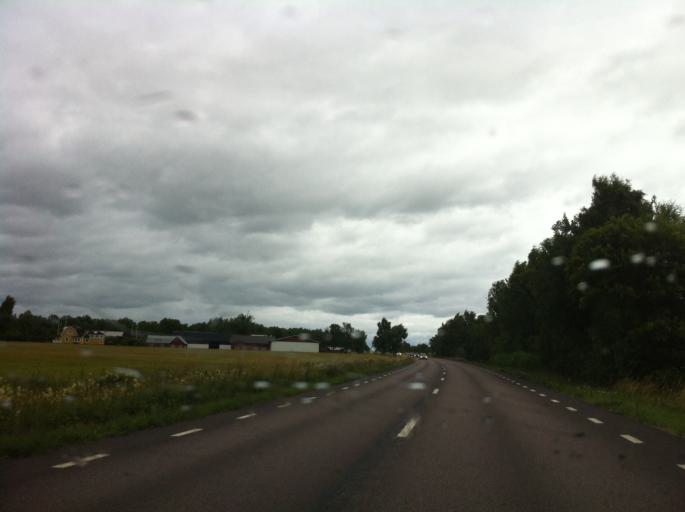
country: SE
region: Kalmar
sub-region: Borgholms Kommun
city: Borgholm
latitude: 57.1094
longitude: 16.9483
